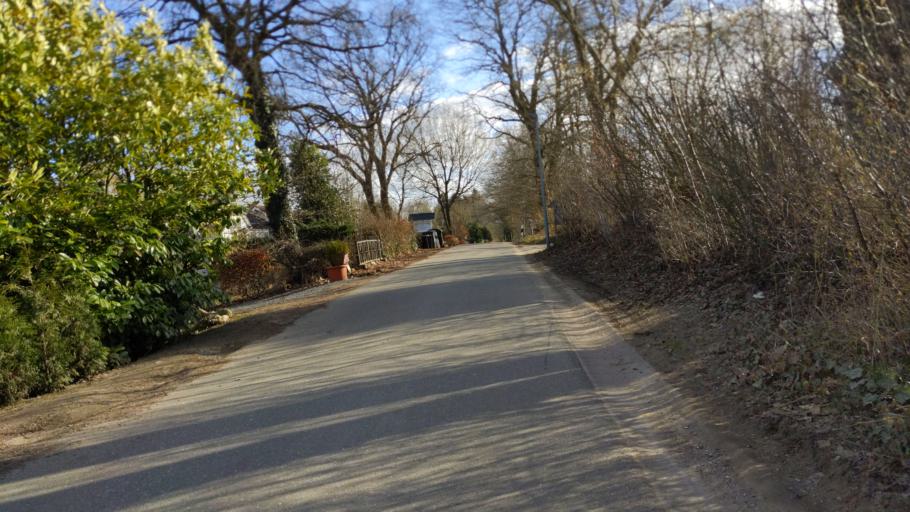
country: DE
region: Schleswig-Holstein
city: Timmendorfer Strand
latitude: 53.9999
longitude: 10.7557
